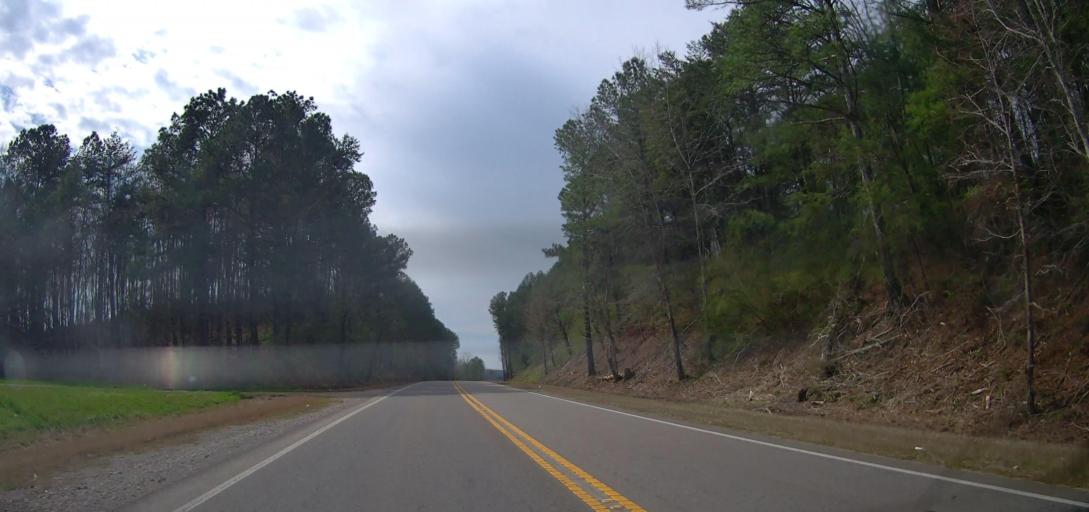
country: US
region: Alabama
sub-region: Walker County
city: Carbon Hill
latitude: 33.8763
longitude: -87.4872
